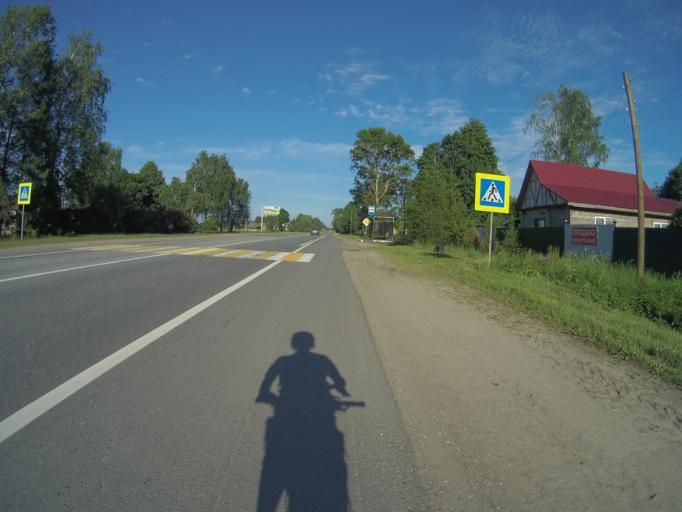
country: RU
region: Vladimir
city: Orgtrud
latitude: 56.1985
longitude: 40.8412
